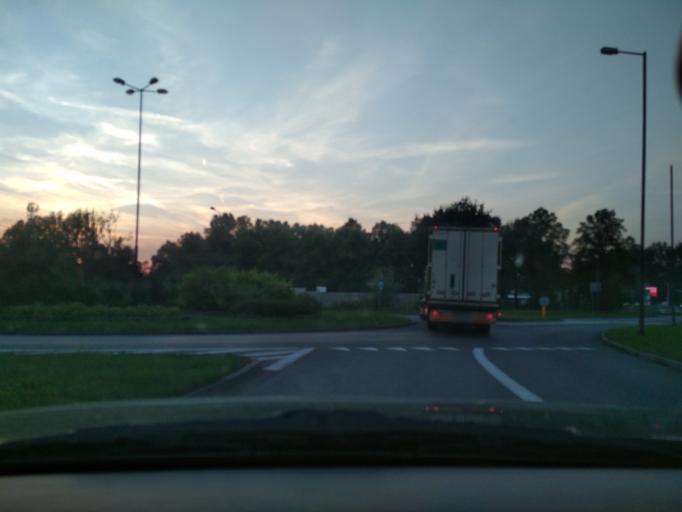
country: PL
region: Silesian Voivodeship
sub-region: Gliwice
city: Gliwice
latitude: 50.2710
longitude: 18.7026
